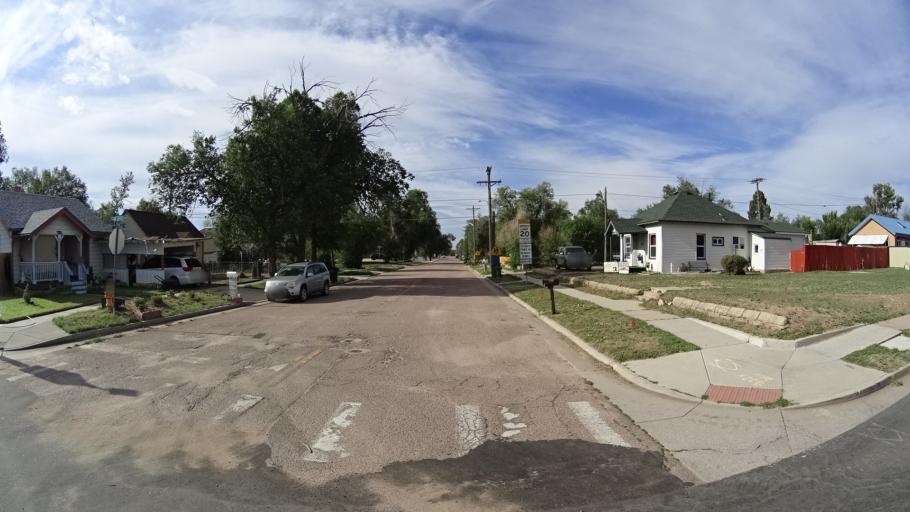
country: US
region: Colorado
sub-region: El Paso County
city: Fountain
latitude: 38.6832
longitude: -104.7021
